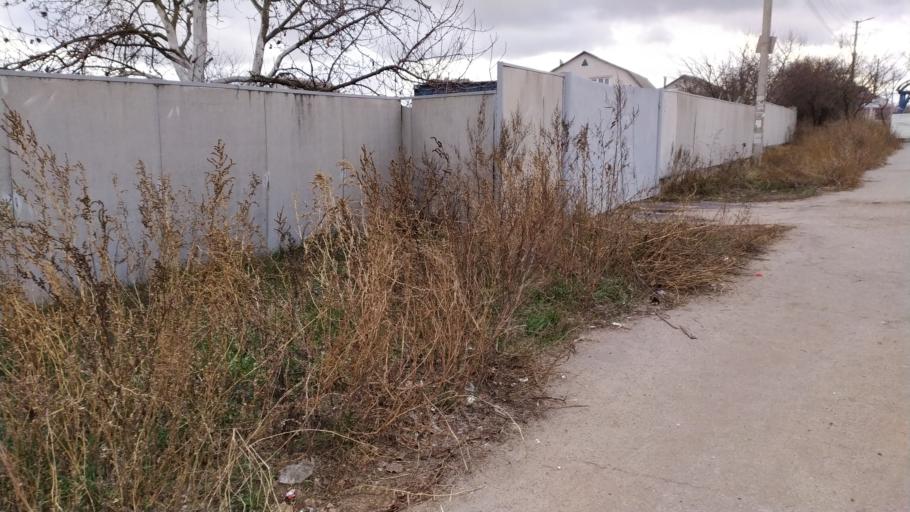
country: RU
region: Kursk
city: Kursk
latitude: 51.6371
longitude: 36.1387
